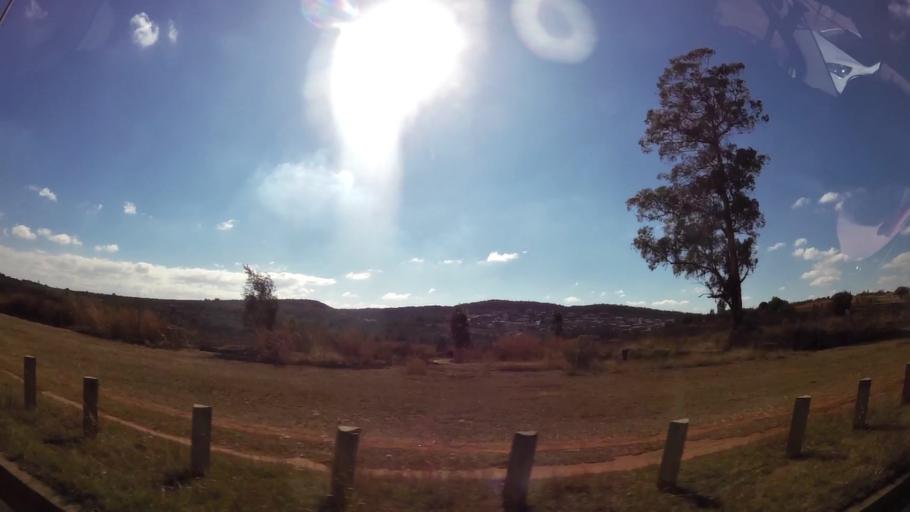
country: ZA
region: Gauteng
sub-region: West Rand District Municipality
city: Krugersdorp
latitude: -26.0907
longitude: 27.8219
